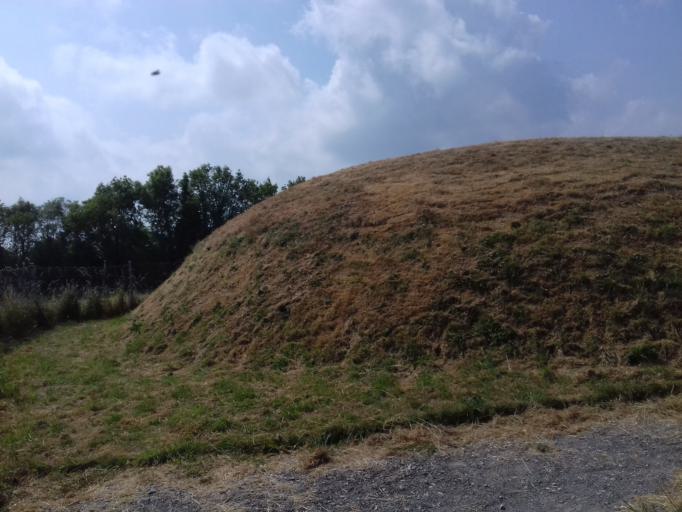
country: IE
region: Leinster
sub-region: An Mhi
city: Stamullin
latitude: 53.5966
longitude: -6.3261
